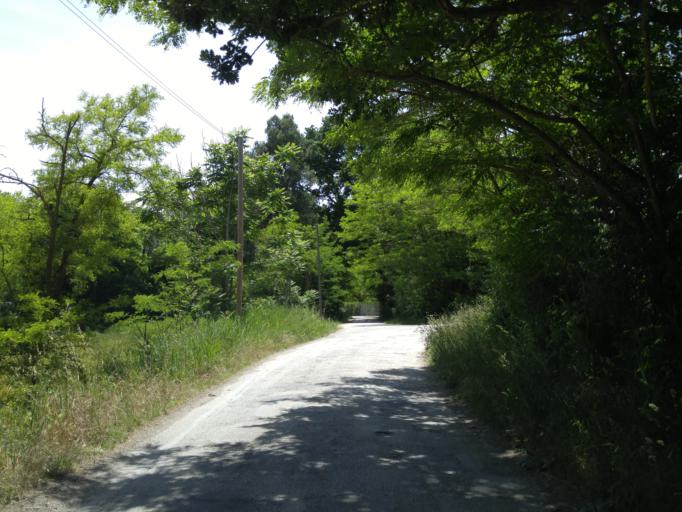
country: IT
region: The Marches
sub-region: Provincia di Pesaro e Urbino
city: Bellocchi
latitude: 43.7720
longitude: 12.9901
